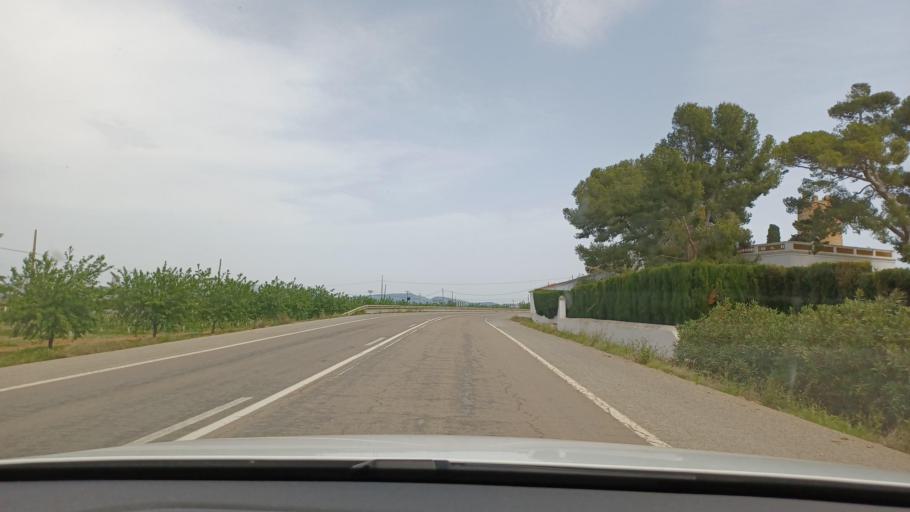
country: ES
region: Catalonia
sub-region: Provincia de Tarragona
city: Amposta
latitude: 40.7324
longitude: 0.5949
